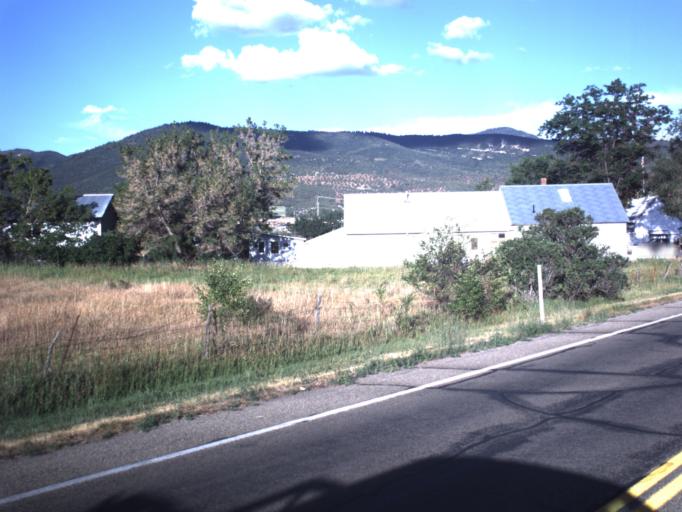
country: US
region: Utah
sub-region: Sanpete County
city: Fairview
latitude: 39.6350
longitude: -111.4422
